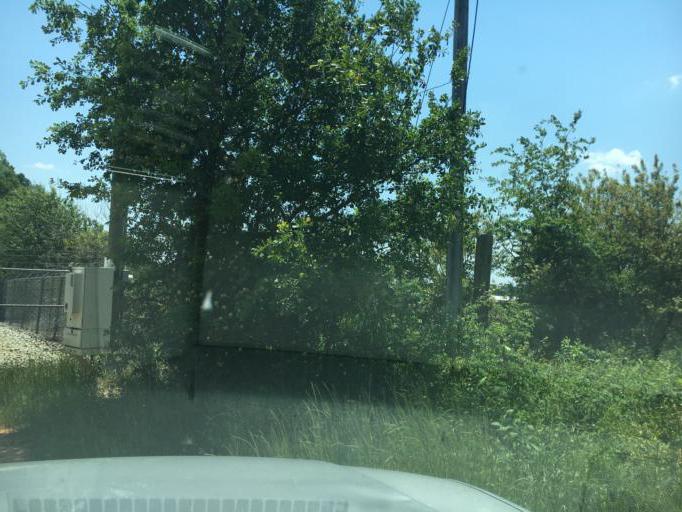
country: US
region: Georgia
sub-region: Hart County
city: Royston
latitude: 34.3606
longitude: -83.0906
